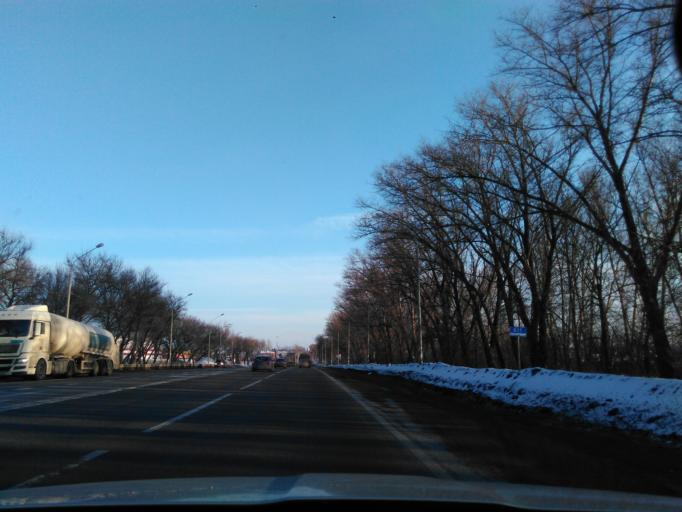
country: RU
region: Moskovskaya
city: Klin
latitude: 56.3636
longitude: 36.6905
